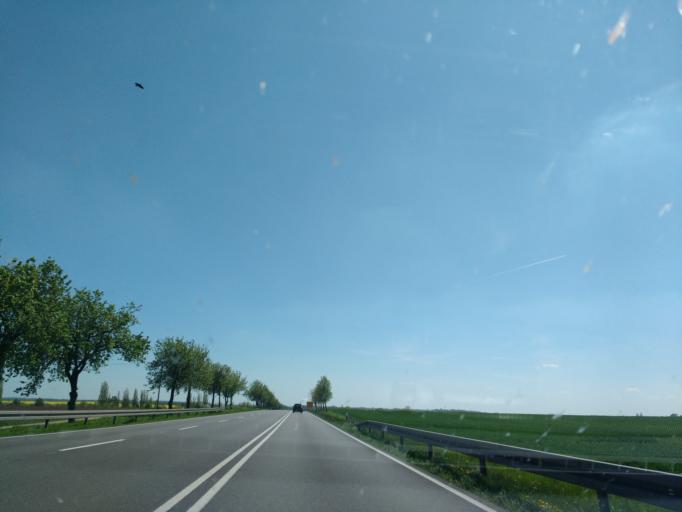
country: DE
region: Saxony-Anhalt
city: Nessa
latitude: 51.1588
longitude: 12.0240
